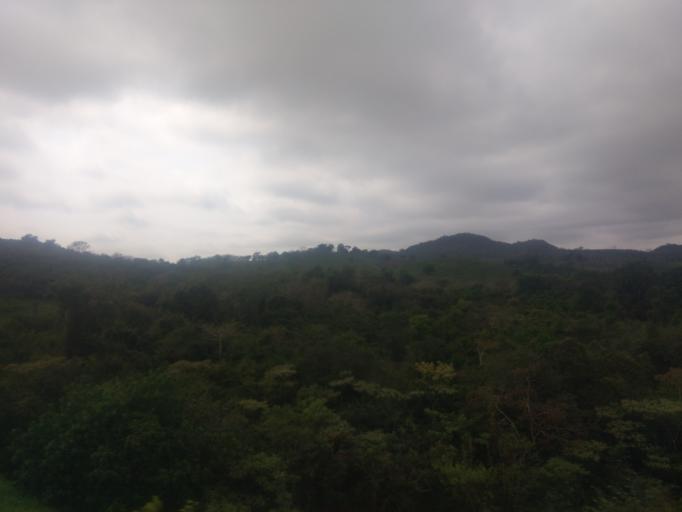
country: MX
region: Veracruz
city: Tihuatlan
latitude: 20.7088
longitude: -97.4885
